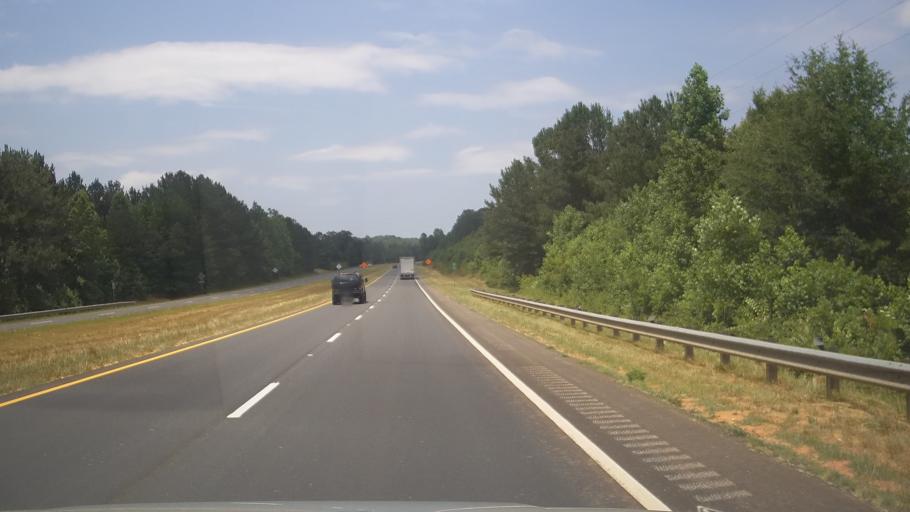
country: US
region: Georgia
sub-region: Jackson County
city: Commerce
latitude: 34.2188
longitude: -83.4457
